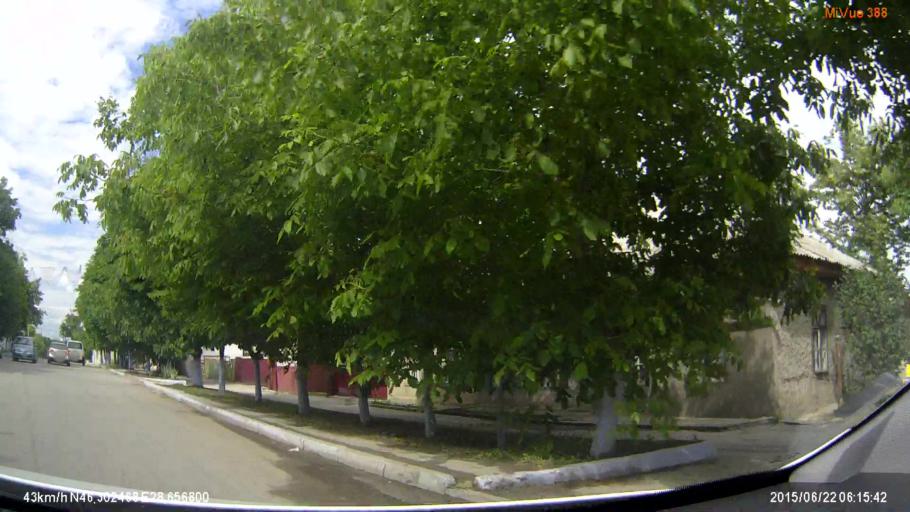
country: MD
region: Gagauzia
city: Comrat
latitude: 46.3023
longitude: 28.6568
